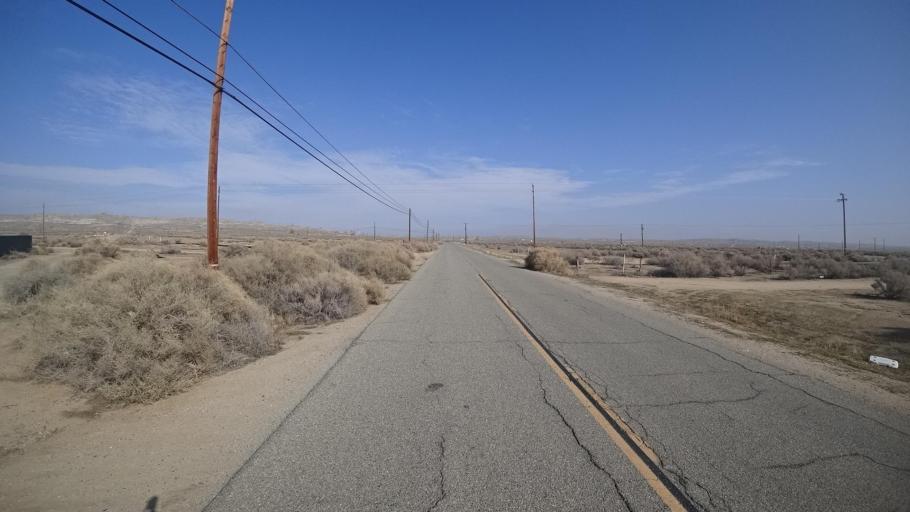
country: US
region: California
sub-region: Kern County
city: Ford City
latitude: 35.1523
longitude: -119.4312
